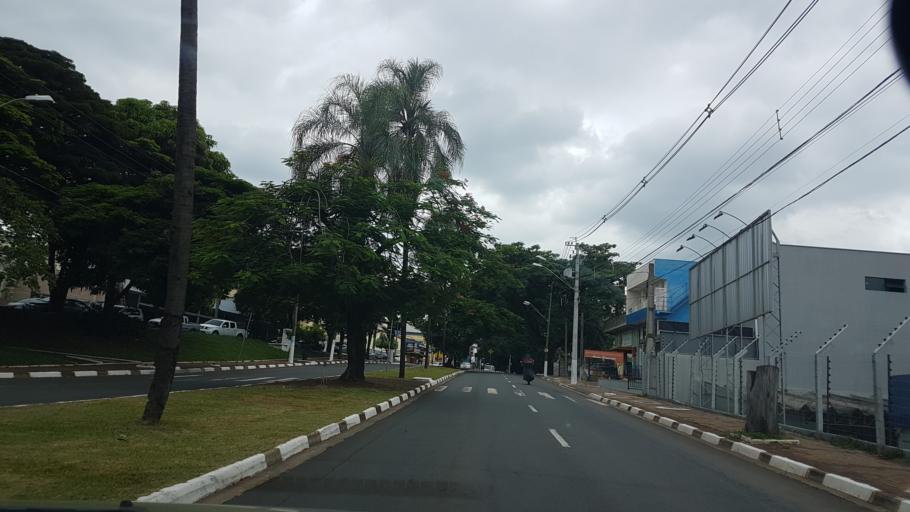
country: BR
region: Sao Paulo
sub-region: Paulinia
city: Paulinia
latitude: -22.7596
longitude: -47.1582
